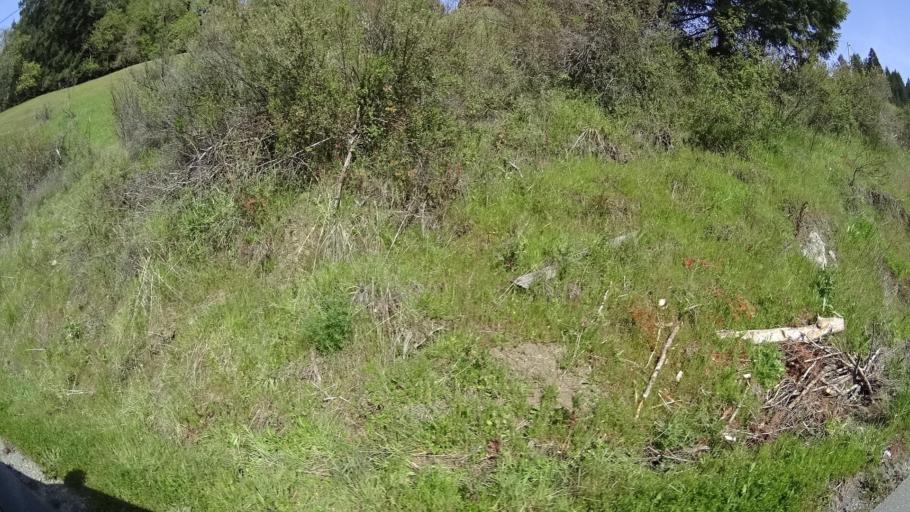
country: US
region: California
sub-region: Humboldt County
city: Redway
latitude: 40.4258
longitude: -123.7658
